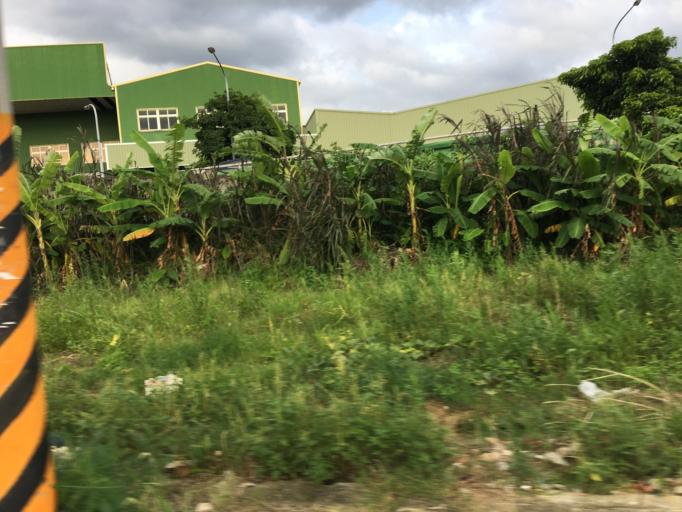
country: TW
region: Taiwan
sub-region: Taichung City
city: Taichung
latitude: 24.0923
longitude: 120.7121
